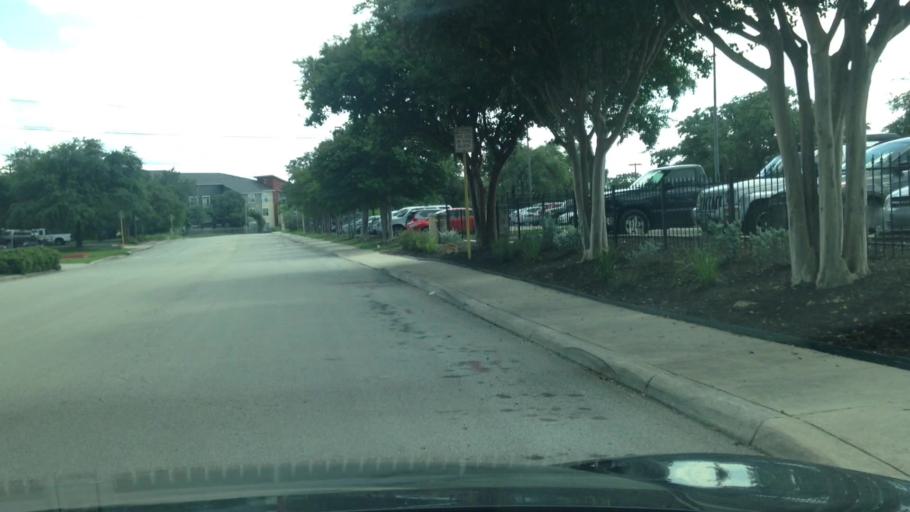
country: US
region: Texas
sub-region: Bexar County
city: Shavano Park
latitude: 29.5452
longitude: -98.5864
